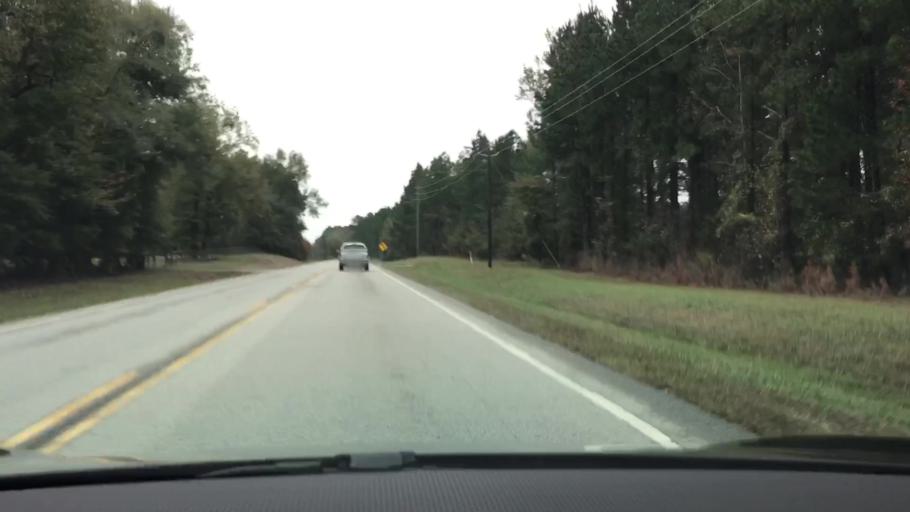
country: US
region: Georgia
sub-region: Warren County
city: Firing Range
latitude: 33.4422
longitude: -82.6924
